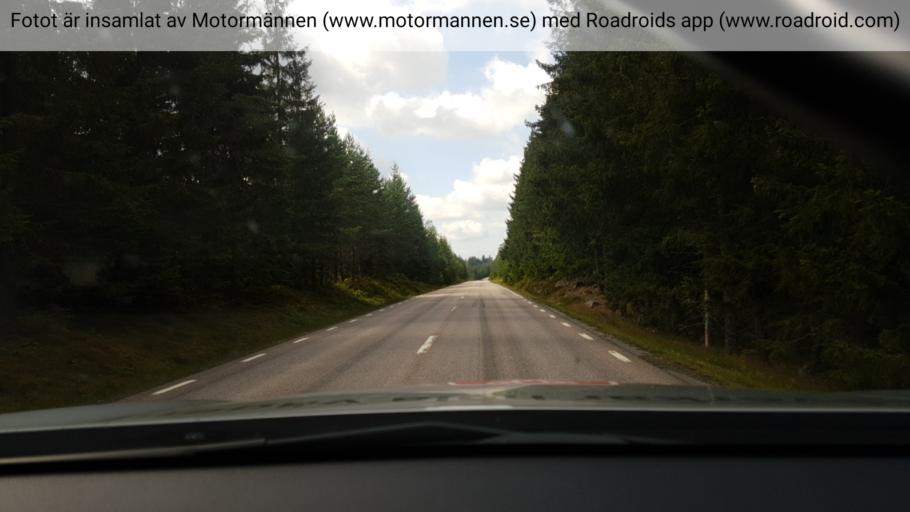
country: SE
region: Vaestra Goetaland
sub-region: Svenljunga Kommun
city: Svenljunga
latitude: 57.4947
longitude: 12.9460
